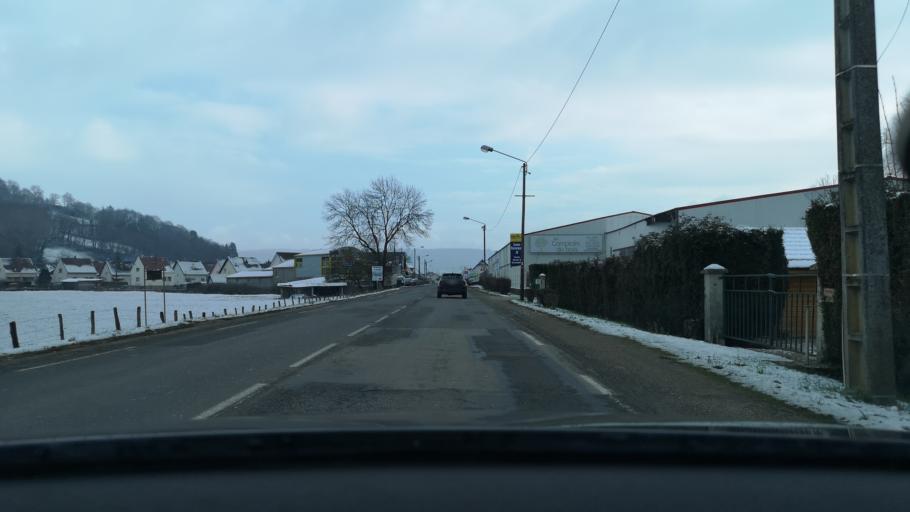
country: FR
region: Franche-Comte
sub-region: Departement du Jura
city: Montmorot
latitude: 46.6771
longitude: 5.5185
